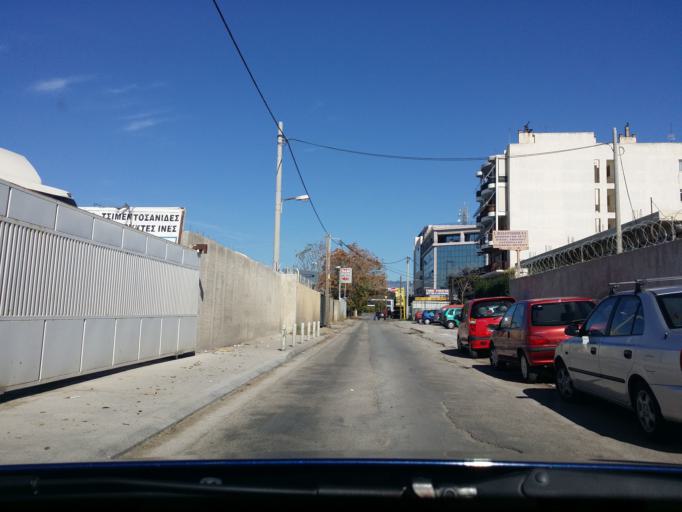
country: GR
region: Attica
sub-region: Nomarchia Athinas
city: Peristeri
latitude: 37.9976
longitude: 23.7008
